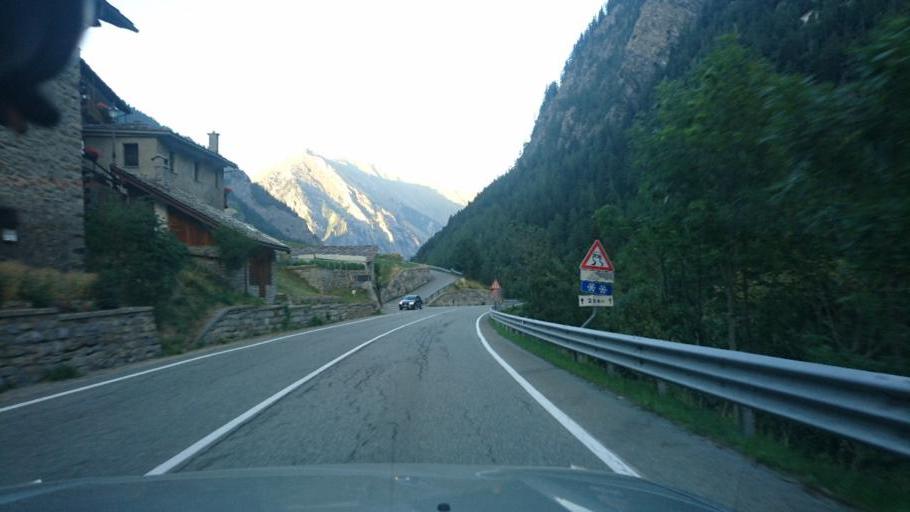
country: IT
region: Aosta Valley
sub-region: Valle d'Aosta
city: Pre Saint Didier
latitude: 45.7427
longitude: 6.9653
